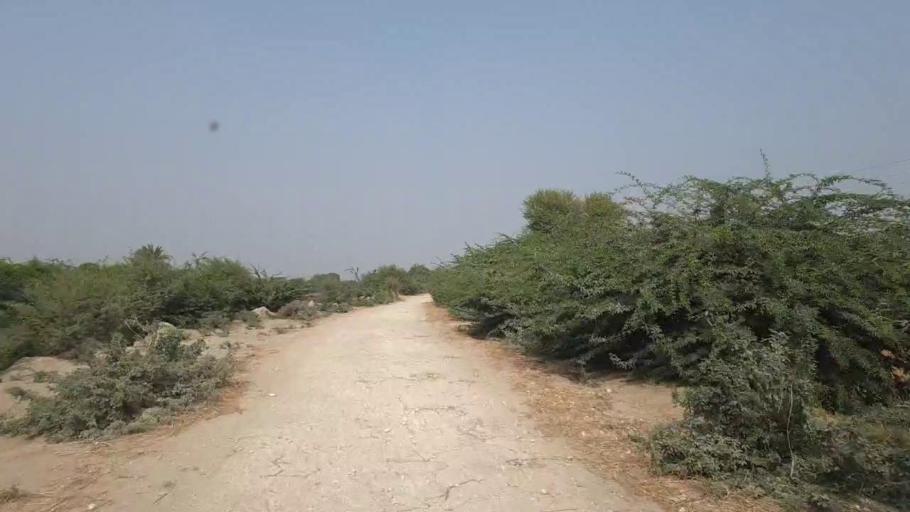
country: PK
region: Sindh
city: Matli
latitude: 24.9337
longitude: 68.6007
